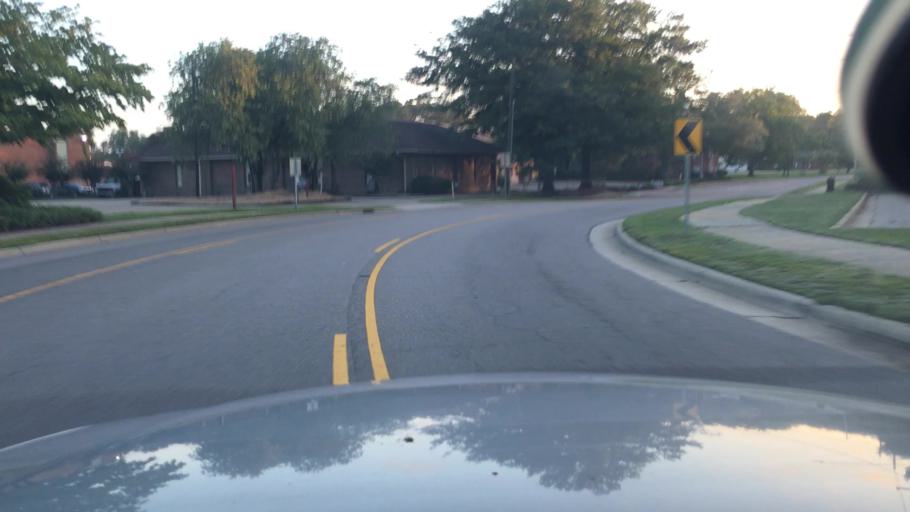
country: US
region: North Carolina
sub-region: Cumberland County
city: Fayetteville
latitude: 35.0682
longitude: -78.9230
